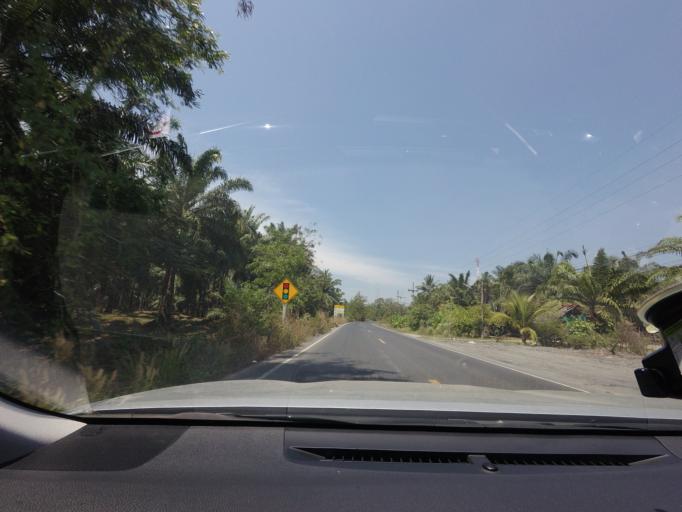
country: TH
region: Surat Thani
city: Tha Chang
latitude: 9.2650
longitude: 99.1593
